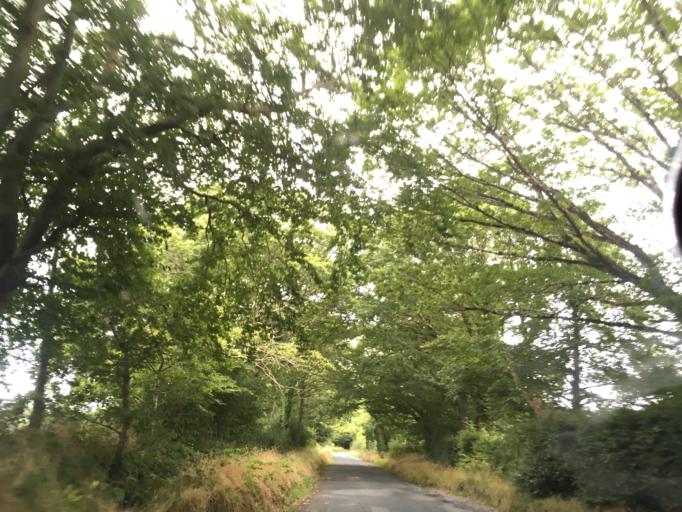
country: IE
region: Leinster
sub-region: Wicklow
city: Rathnew
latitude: 52.9189
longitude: -6.1076
